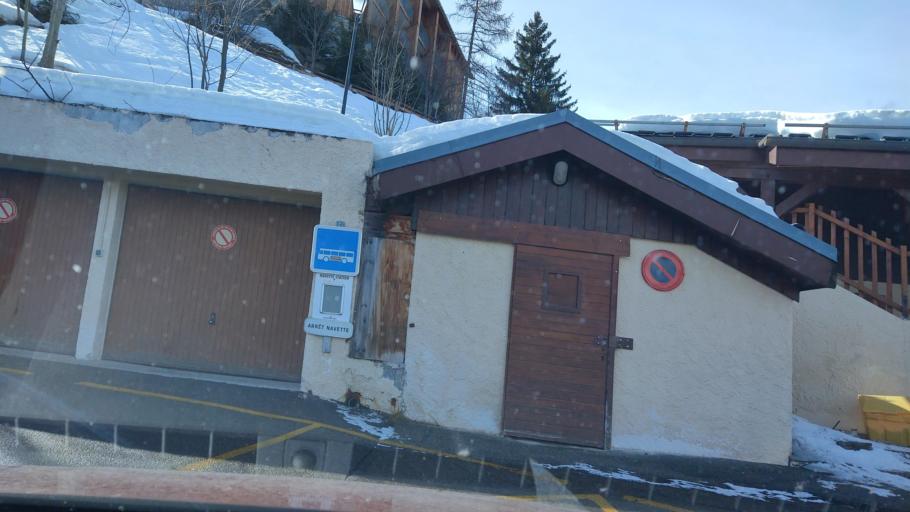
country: FR
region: Rhone-Alpes
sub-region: Departement de la Savoie
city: Belle-Plagne
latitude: 45.5588
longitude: 6.7391
